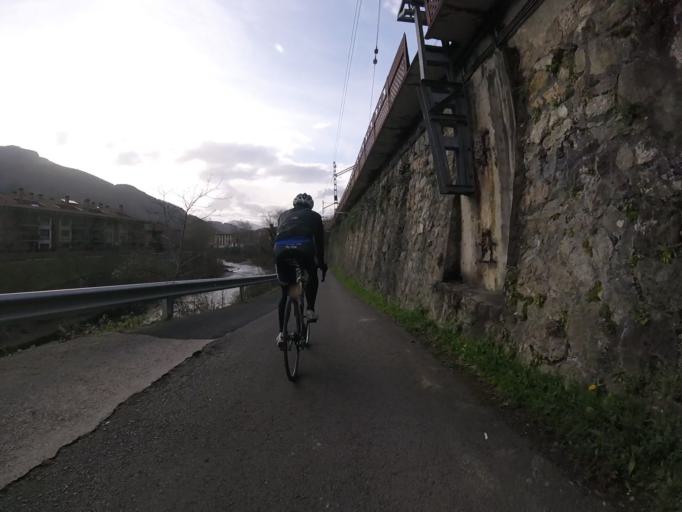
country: ES
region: Basque Country
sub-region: Provincia de Guipuzcoa
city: Irura
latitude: 43.1666
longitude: -2.0717
